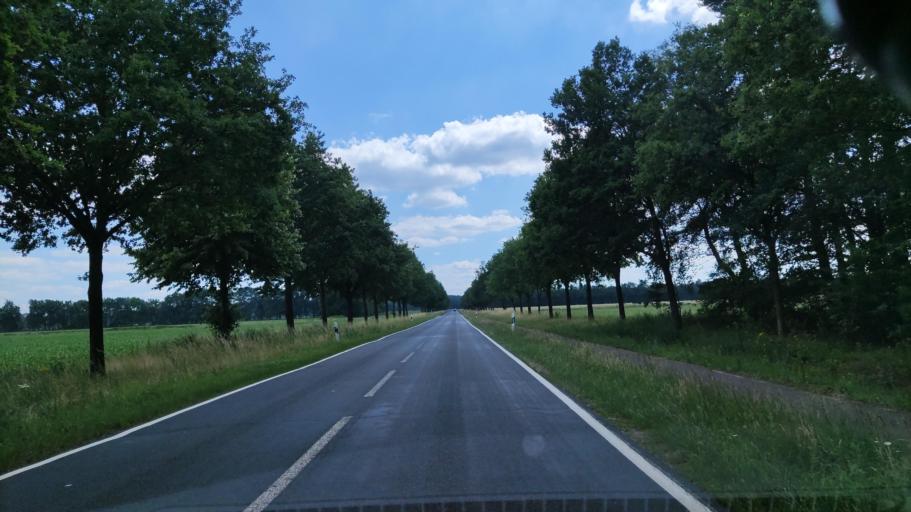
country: DE
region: Mecklenburg-Vorpommern
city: Lubtheen
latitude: 53.3308
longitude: 11.1312
